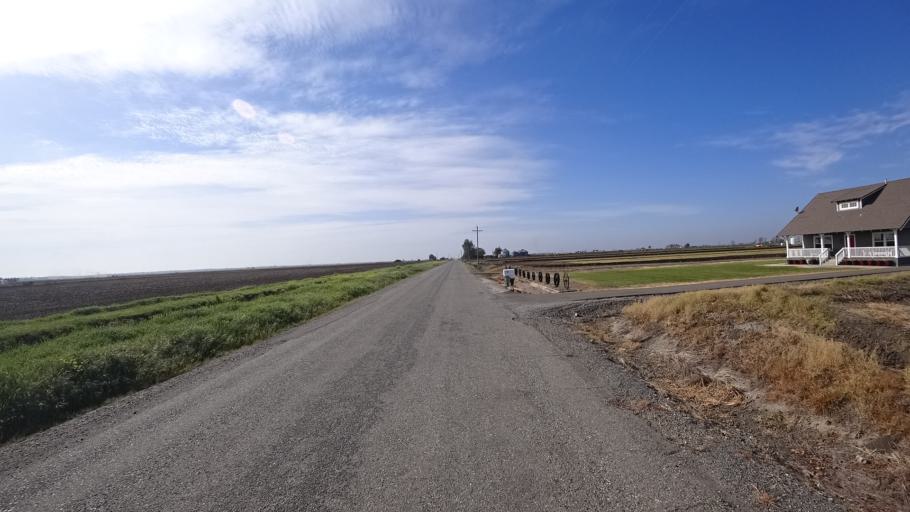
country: US
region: California
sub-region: Glenn County
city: Willows
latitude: 39.5759
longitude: -122.0463
